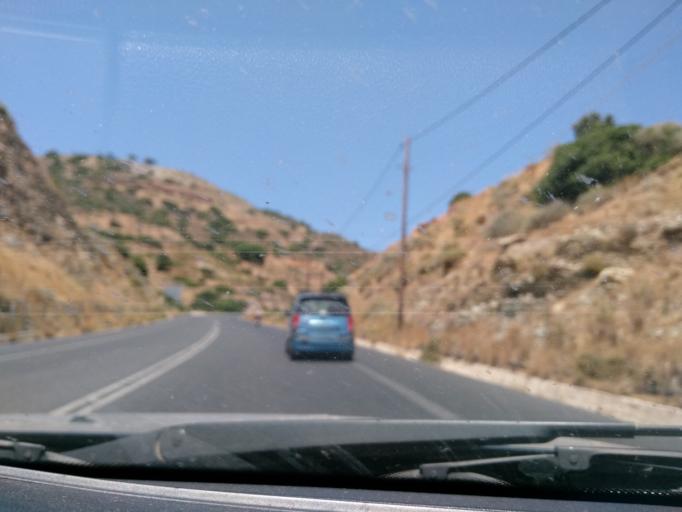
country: GR
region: Crete
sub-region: Nomos Irakleiou
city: Gazi
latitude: 35.3710
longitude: 25.0375
